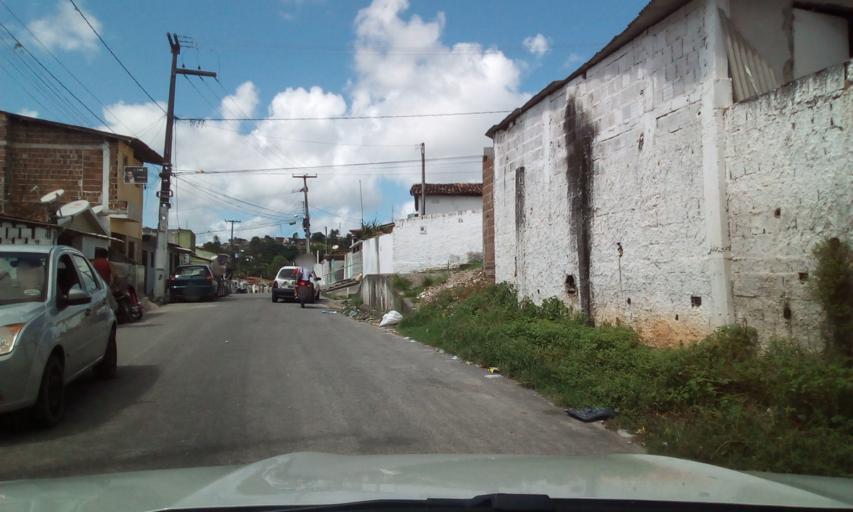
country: BR
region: Paraiba
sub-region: Bayeux
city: Bayeux
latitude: -7.1326
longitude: -34.9217
